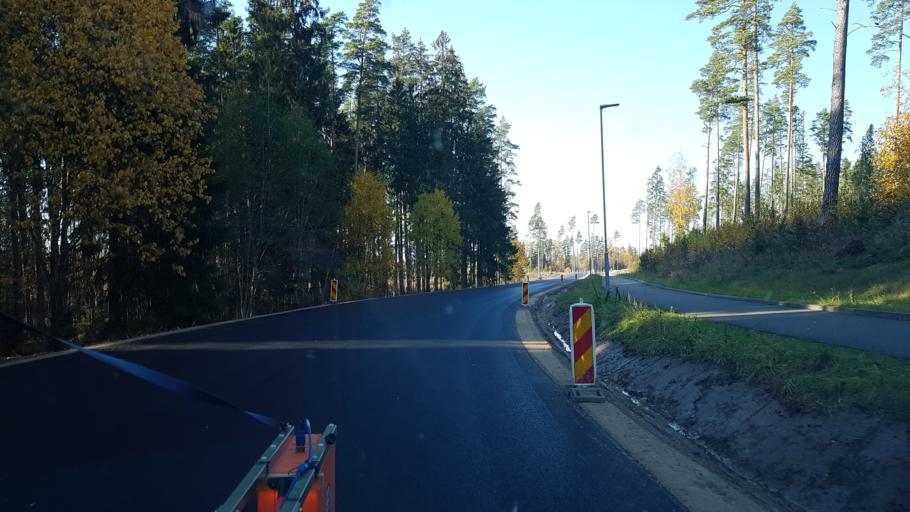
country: EE
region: Vorumaa
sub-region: Antsla vald
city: Vana-Antsla
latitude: 57.8313
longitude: 26.5123
